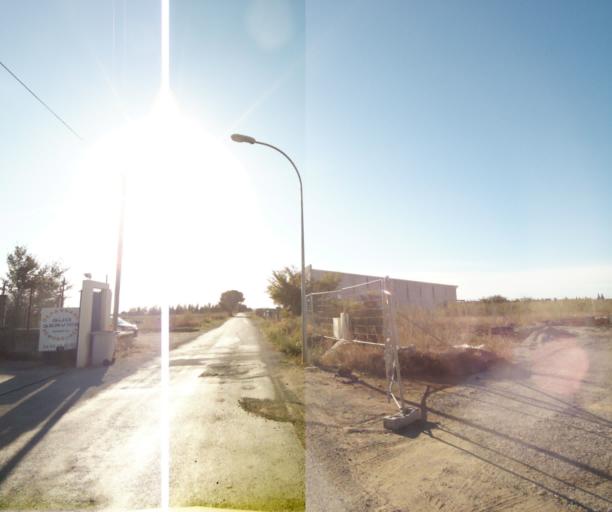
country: FR
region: Languedoc-Roussillon
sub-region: Departement du Gard
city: Bouillargues
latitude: 43.7907
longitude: 4.4396
